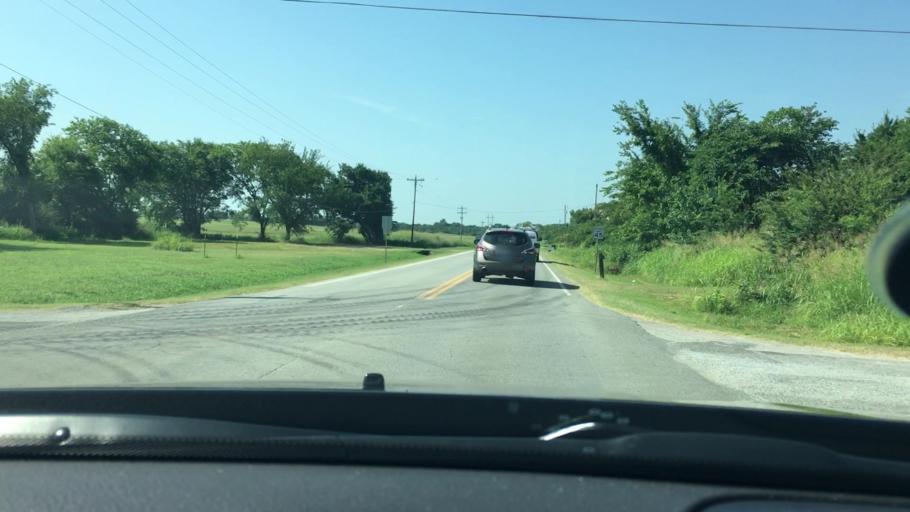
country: US
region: Oklahoma
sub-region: Coal County
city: Coalgate
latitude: 34.6007
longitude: -96.4244
